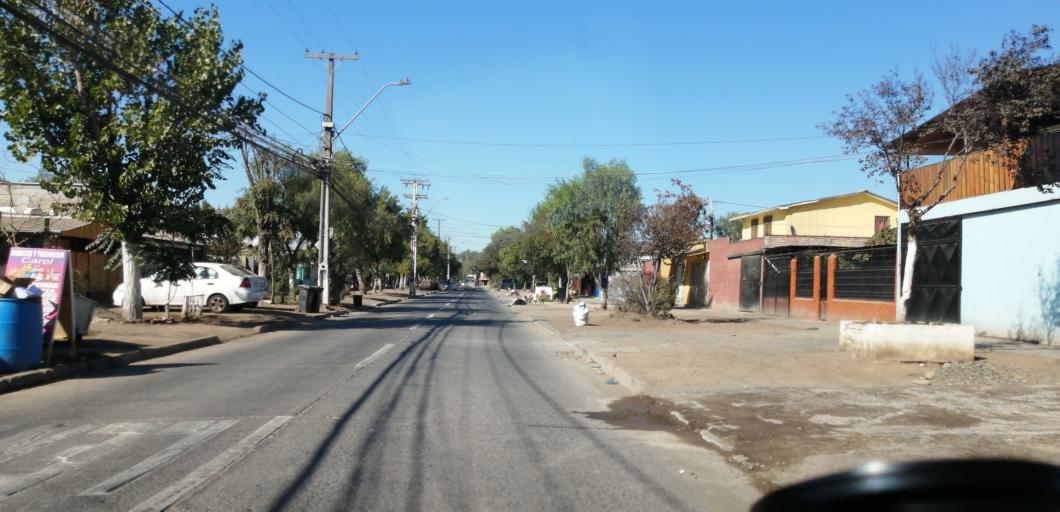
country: CL
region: Santiago Metropolitan
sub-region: Provincia de Santiago
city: Lo Prado
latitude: -33.4287
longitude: -70.7580
